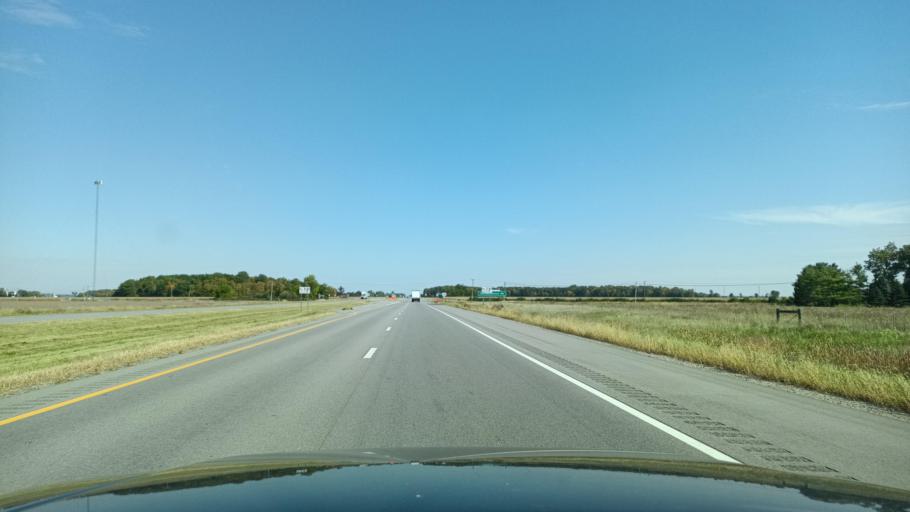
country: US
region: Ohio
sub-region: Defiance County
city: Defiance
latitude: 41.3307
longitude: -84.2881
